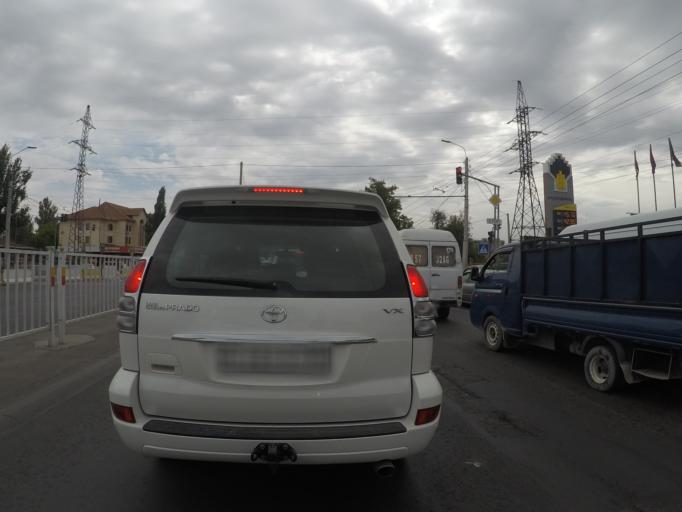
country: KG
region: Chuy
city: Bishkek
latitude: 42.8849
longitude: 74.5684
